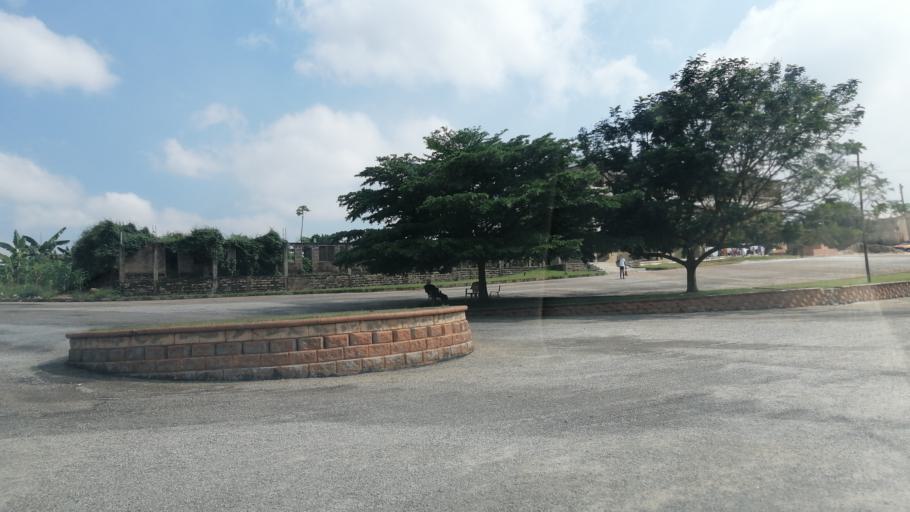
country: GH
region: Ashanti
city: Kumasi
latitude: 6.7010
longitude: -1.6773
